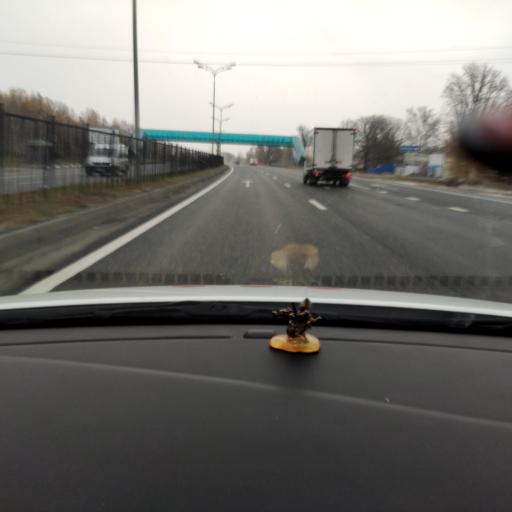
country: RU
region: Tatarstan
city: Osinovo
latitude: 55.8649
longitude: 48.7699
